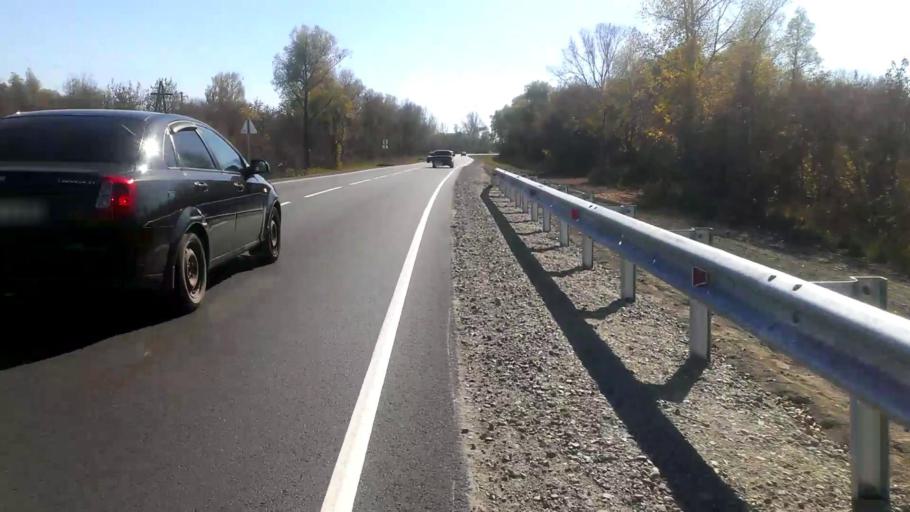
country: RU
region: Altai Krai
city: Sannikovo
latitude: 53.3266
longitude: 83.9417
